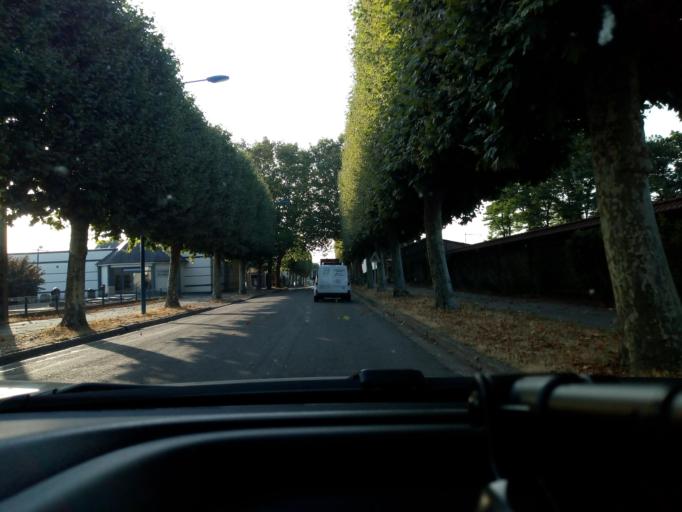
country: FR
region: Haute-Normandie
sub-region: Departement de la Seine-Maritime
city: Sotteville-les-Rouen
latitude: 49.4100
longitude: 1.0812
